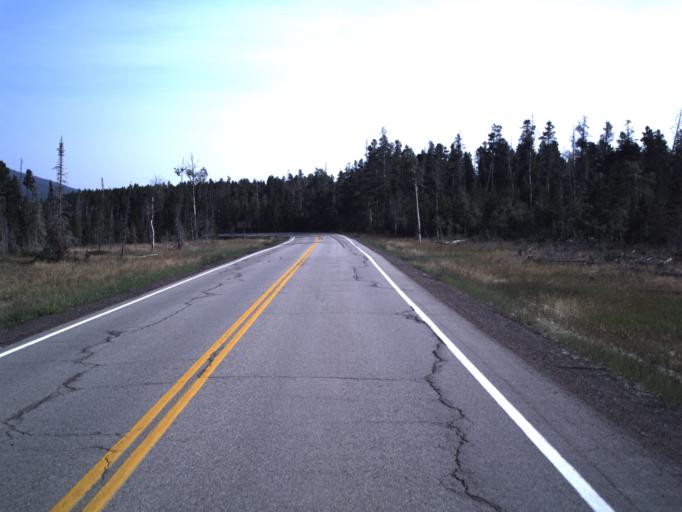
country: US
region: Utah
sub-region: Uintah County
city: Maeser
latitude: 40.7546
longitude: -109.4704
